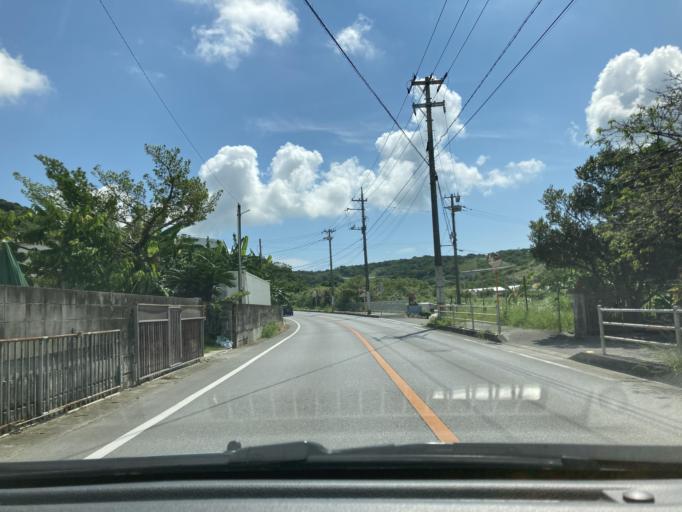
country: JP
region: Okinawa
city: Tomigusuku
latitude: 26.1629
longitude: 127.7608
